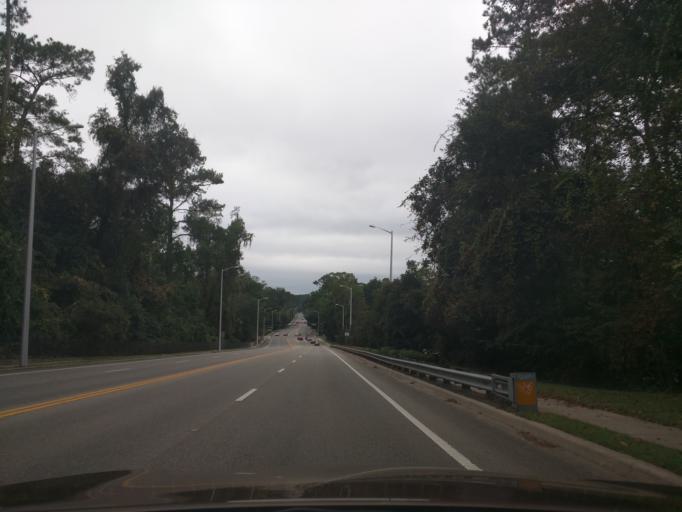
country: US
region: Florida
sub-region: Leon County
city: Tallahassee
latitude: 30.4420
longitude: -84.2383
